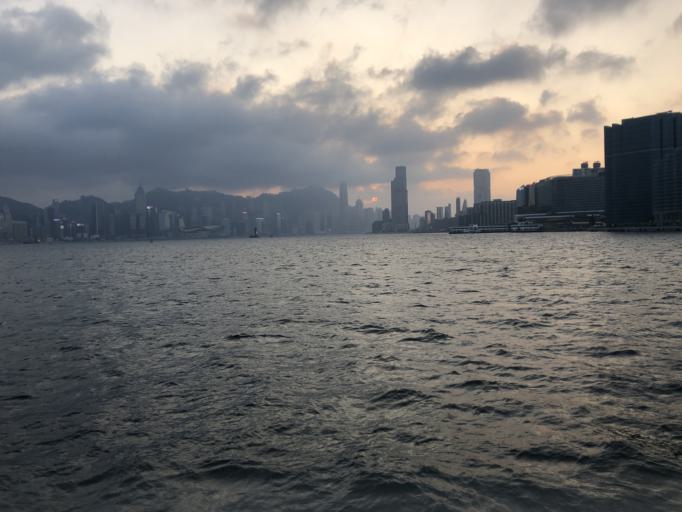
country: HK
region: Kowloon City
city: Kowloon
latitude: 22.3020
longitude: 114.1971
